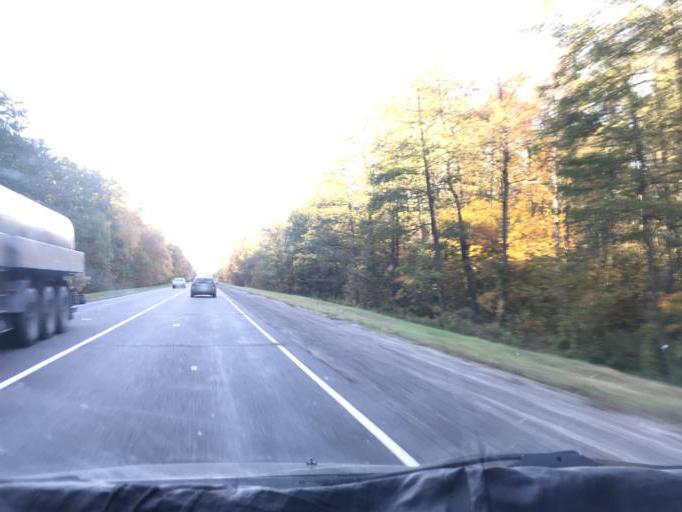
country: BY
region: Gomel
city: Pyetrykaw
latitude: 52.2724
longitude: 28.2668
